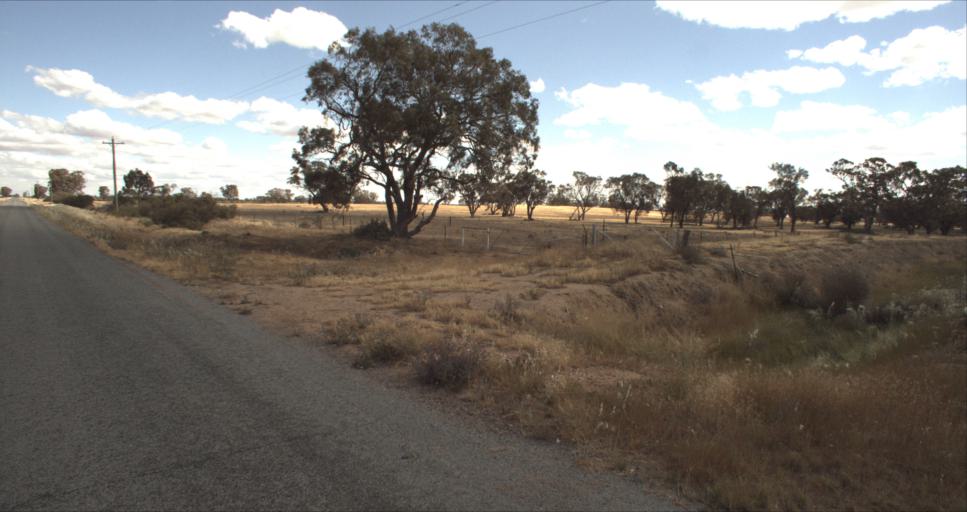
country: AU
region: New South Wales
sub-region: Leeton
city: Leeton
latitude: -34.4879
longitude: 146.2478
